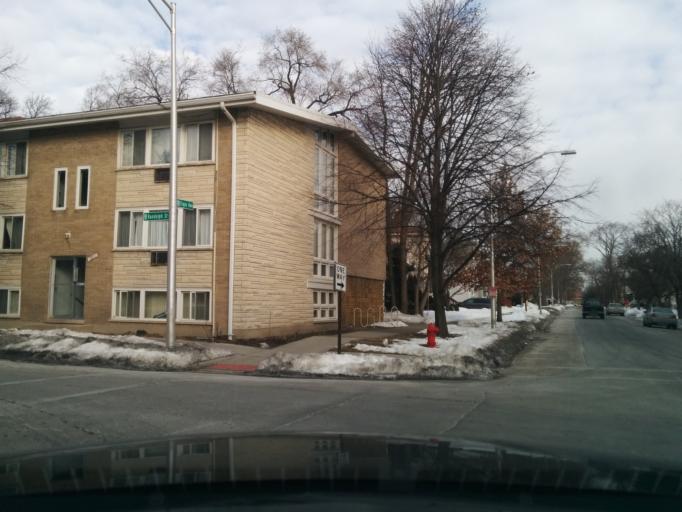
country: US
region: Illinois
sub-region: Cook County
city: Forest Park
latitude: 41.8832
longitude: -87.8062
